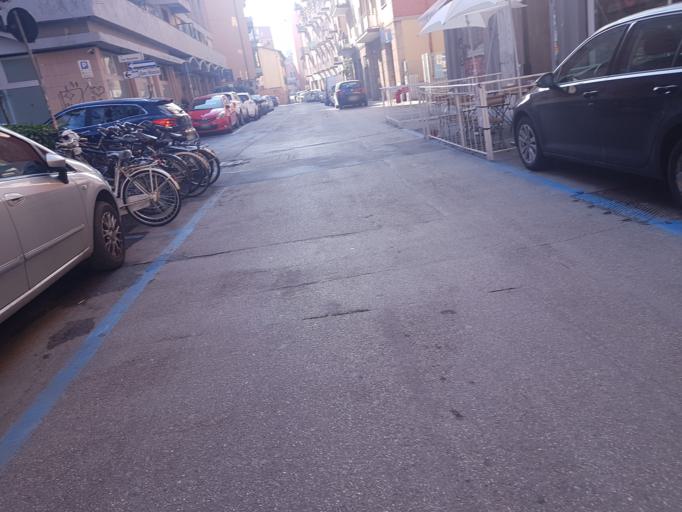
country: IT
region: Emilia-Romagna
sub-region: Provincia di Bologna
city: Bologna
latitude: 44.4969
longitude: 11.3297
